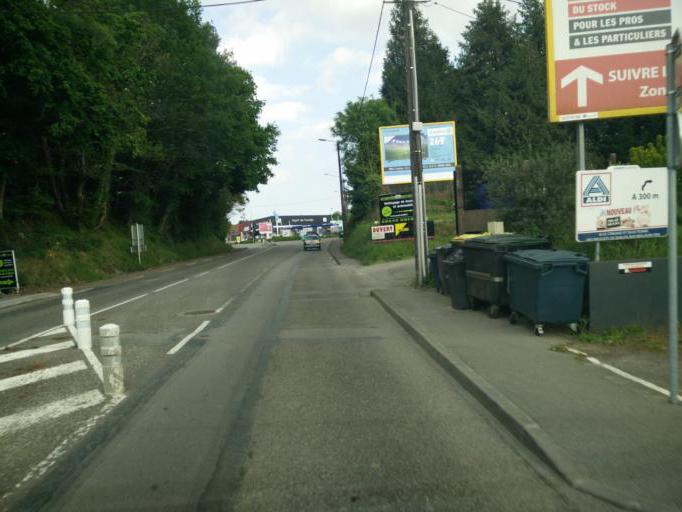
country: FR
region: Brittany
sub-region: Departement du Finistere
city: Quimperle
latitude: 47.8666
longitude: -3.5344
